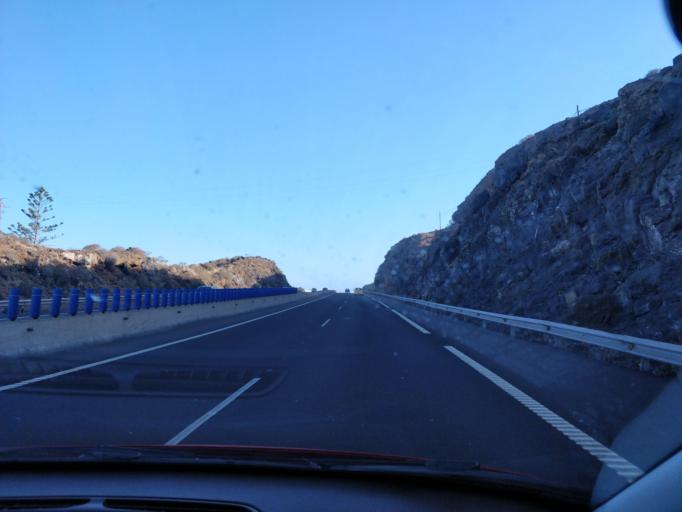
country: ES
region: Canary Islands
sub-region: Provincia de Santa Cruz de Tenerife
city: Fasnia
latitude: 28.2583
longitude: -16.3955
